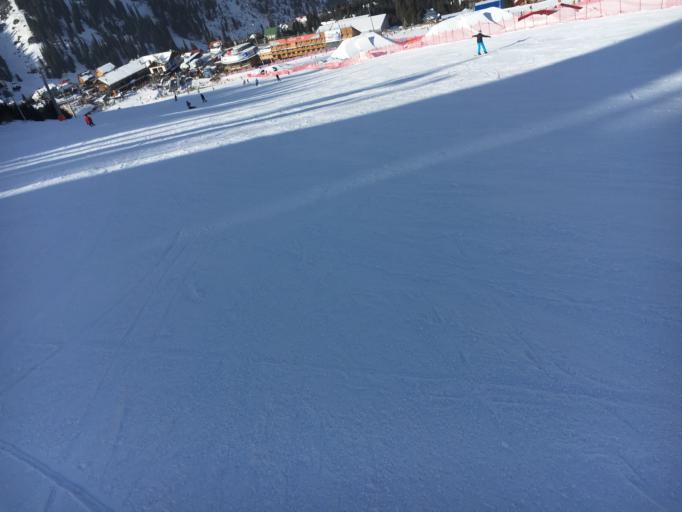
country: KZ
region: Almaty Qalasy
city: Almaty
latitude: 43.1258
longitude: 77.0864
